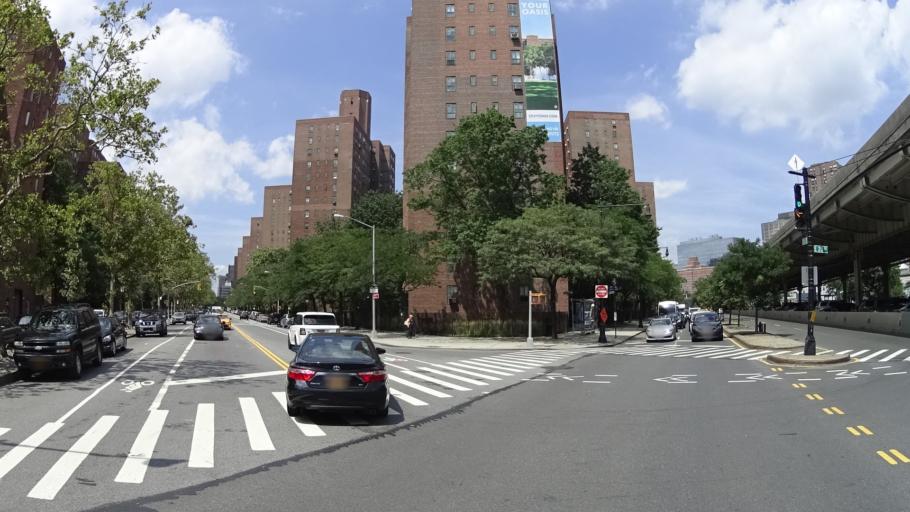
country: US
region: New York
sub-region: Queens County
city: Long Island City
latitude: 40.7328
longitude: -73.9746
